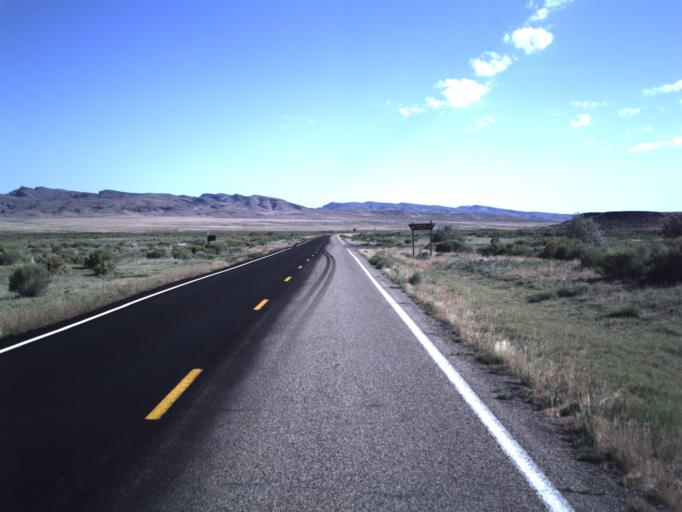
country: US
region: Utah
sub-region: Beaver County
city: Milford
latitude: 38.7183
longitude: -112.9687
